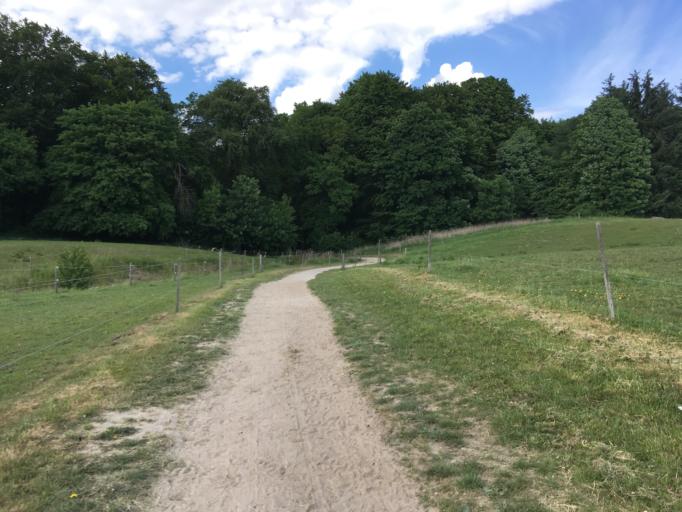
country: DK
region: Capital Region
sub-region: Ballerup Kommune
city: Ballerup
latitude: 55.7537
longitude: 12.3686
